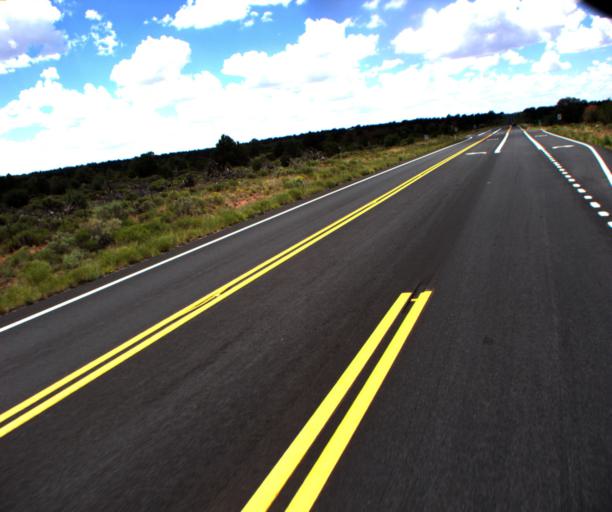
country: US
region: Arizona
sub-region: Coconino County
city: Parks
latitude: 35.6040
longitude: -112.0389
